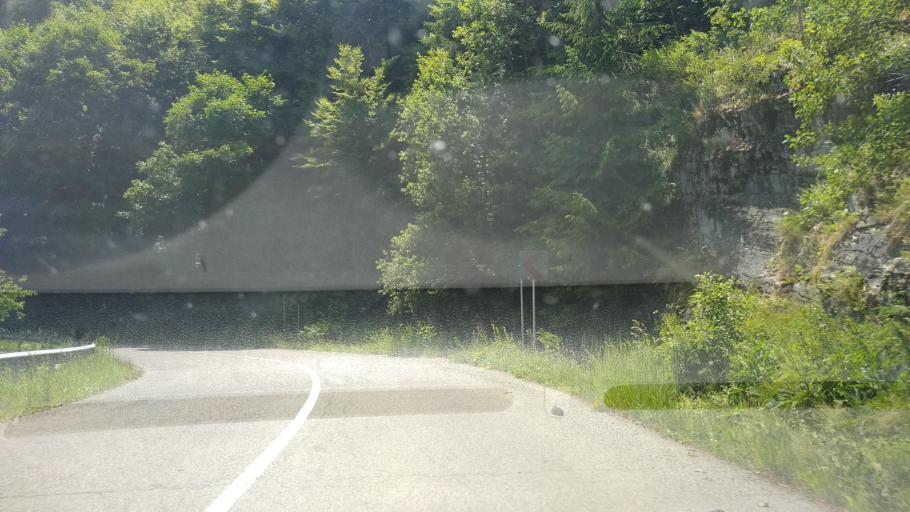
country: RO
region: Hunedoara
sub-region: Comuna Uricani
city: Uricani
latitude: 45.2804
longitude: 22.9643
